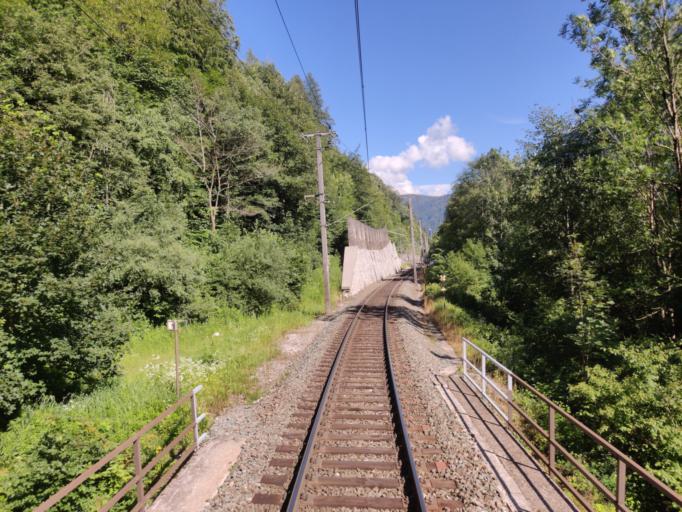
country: AT
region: Vorarlberg
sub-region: Politischer Bezirk Bludenz
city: Innerbraz
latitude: 47.1416
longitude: 9.9421
